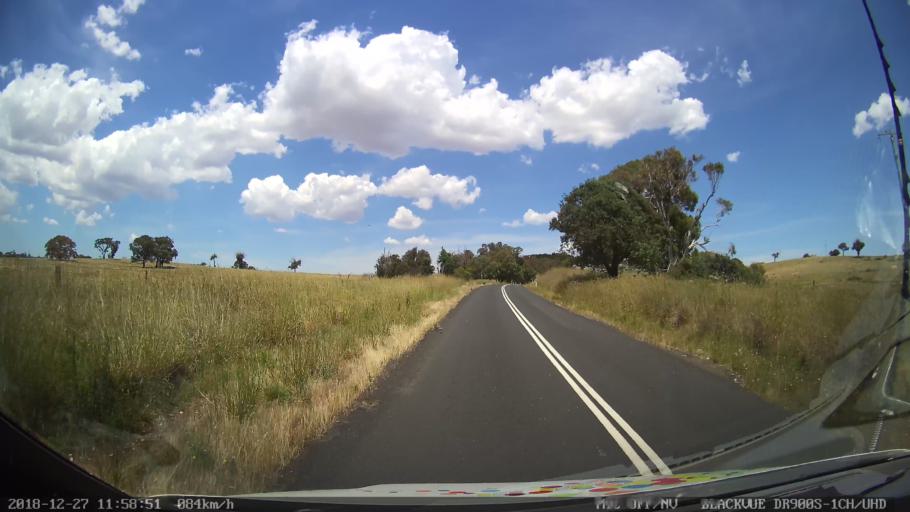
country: AU
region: New South Wales
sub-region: Blayney
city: Blayney
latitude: -33.7291
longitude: 149.3821
